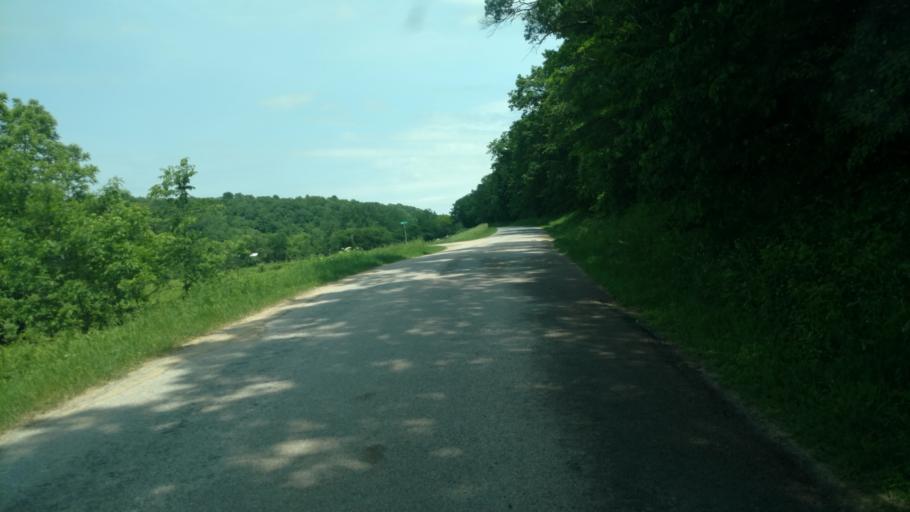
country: US
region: Wisconsin
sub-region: Monroe County
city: Cashton
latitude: 43.6783
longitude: -90.6922
